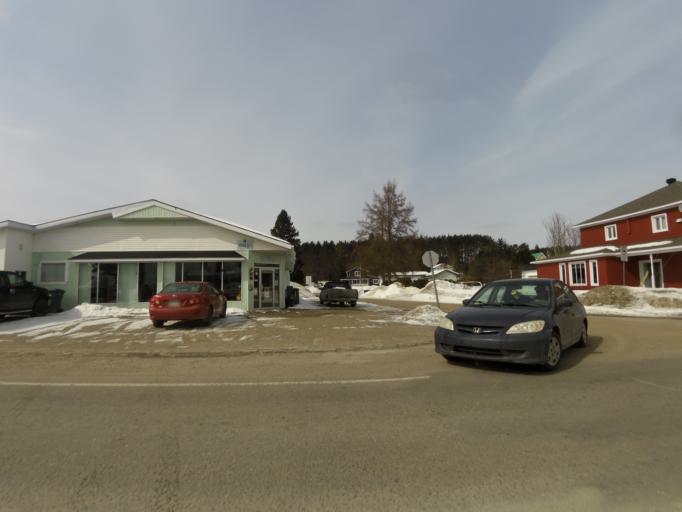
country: CA
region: Quebec
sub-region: Laurentides
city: Ferme-Neuve
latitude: 46.7789
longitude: -75.3384
